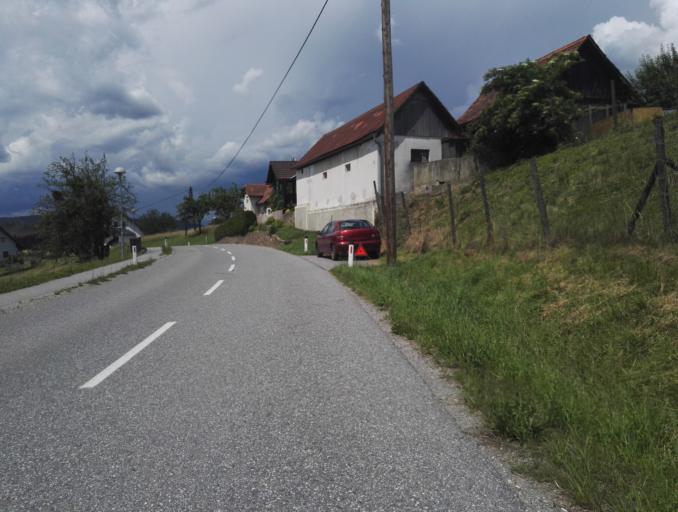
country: AT
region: Styria
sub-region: Politischer Bezirk Graz-Umgebung
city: Sankt Oswald bei Plankenwarth
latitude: 47.0893
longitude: 15.2833
